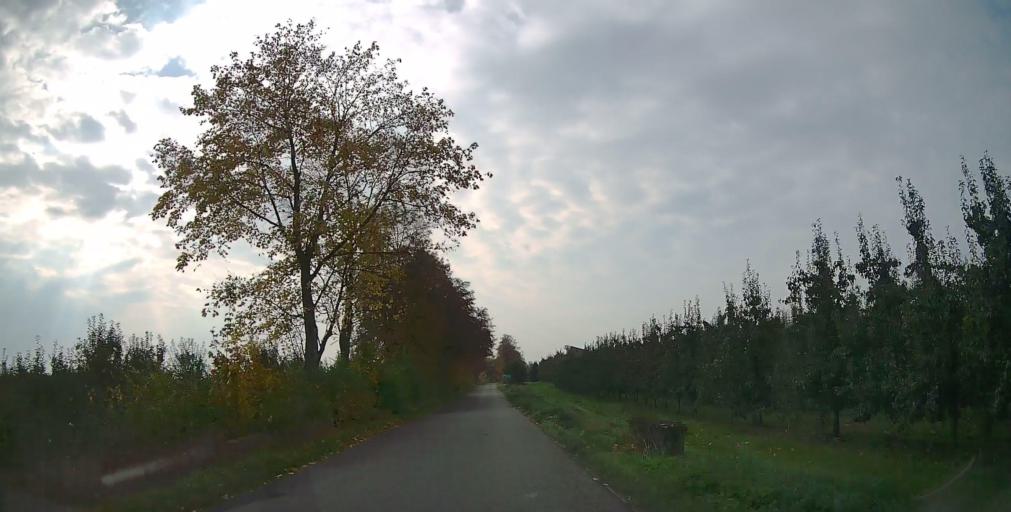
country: PL
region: Masovian Voivodeship
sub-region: Powiat grojecki
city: Mogielnica
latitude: 51.6780
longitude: 20.7140
